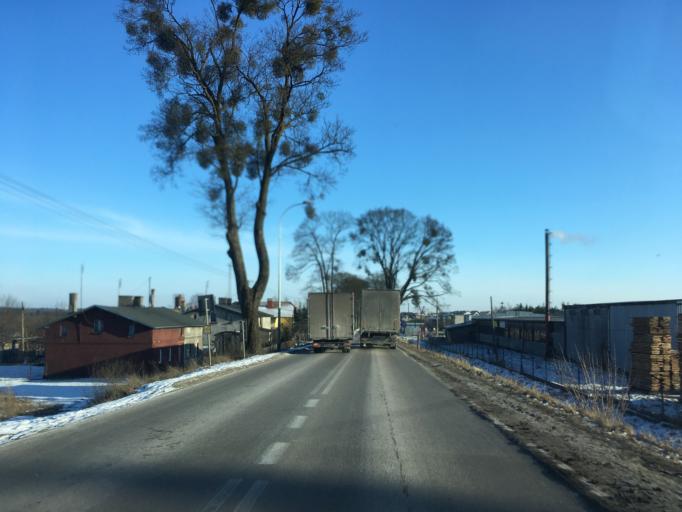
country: PL
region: Pomeranian Voivodeship
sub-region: Powiat starogardzki
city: Zblewo
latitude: 53.9453
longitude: 18.3121
